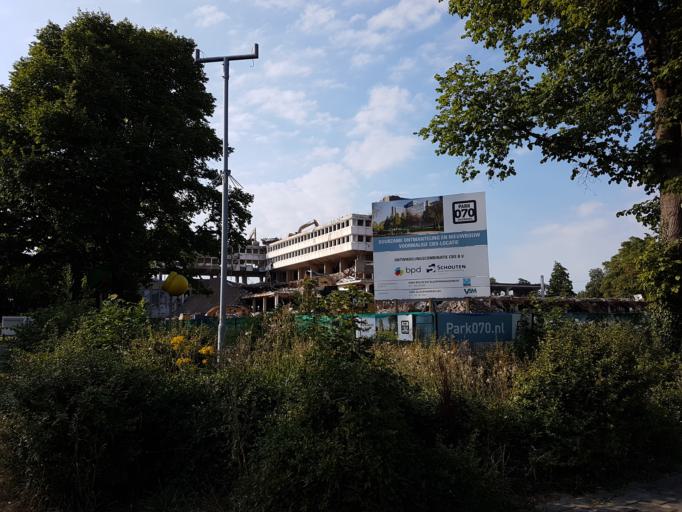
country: NL
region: South Holland
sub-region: Gemeente Leidschendam-Voorburg
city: Voorburg
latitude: 52.0819
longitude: 4.3572
